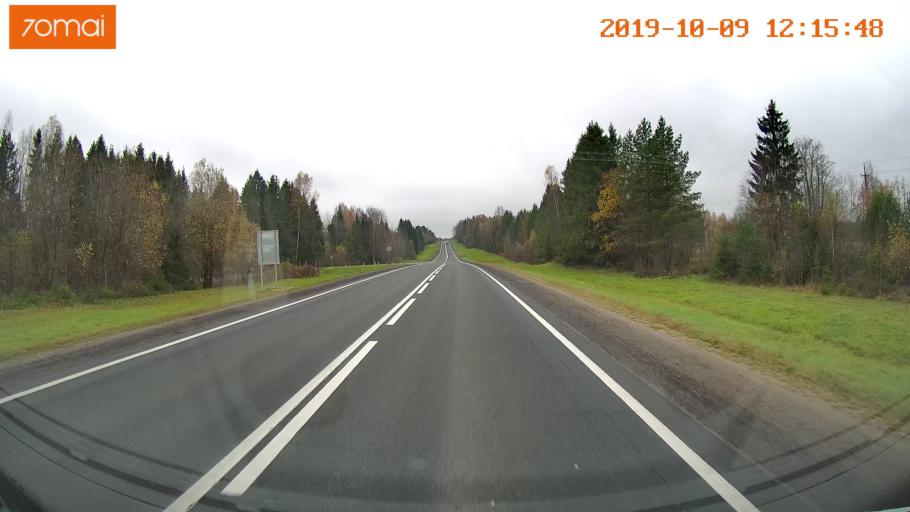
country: RU
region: Jaroslavl
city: Prechistoye
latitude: 58.4779
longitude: 40.3224
